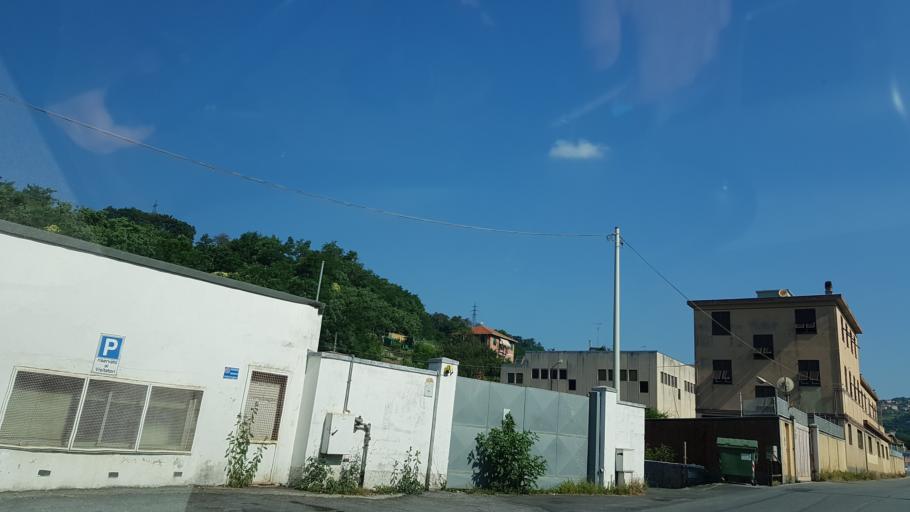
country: IT
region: Liguria
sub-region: Provincia di Genova
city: Manesseno
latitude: 44.4857
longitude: 8.9214
